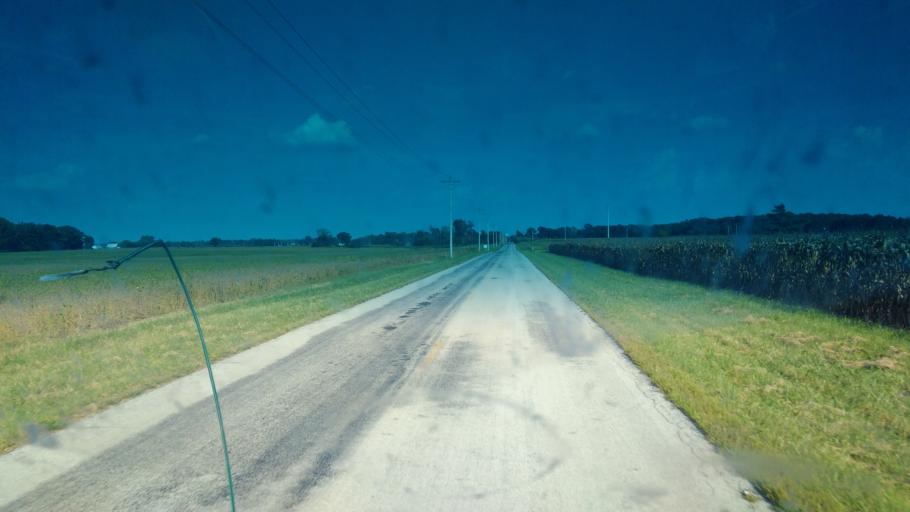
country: US
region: Ohio
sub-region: Wyandot County
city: Carey
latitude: 40.9051
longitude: -83.3955
